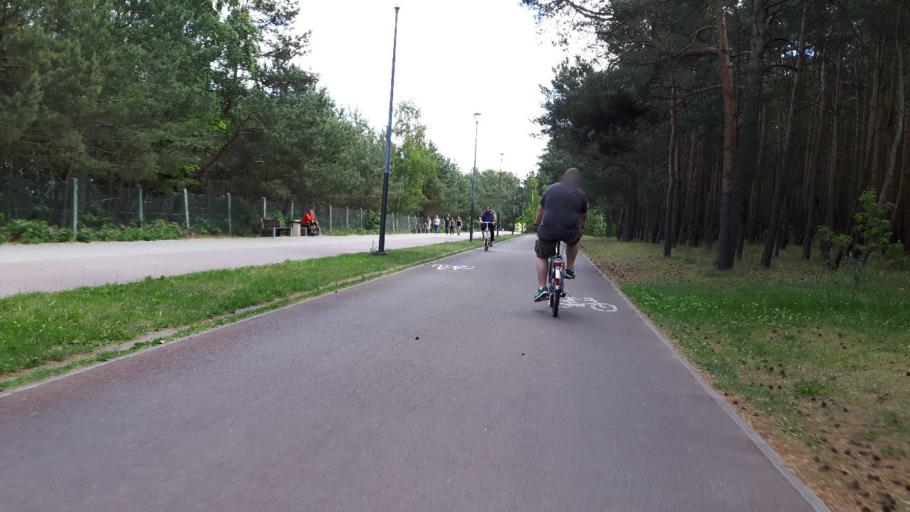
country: PL
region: Pomeranian Voivodeship
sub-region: Sopot
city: Sopot
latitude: 54.4198
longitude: 18.6085
